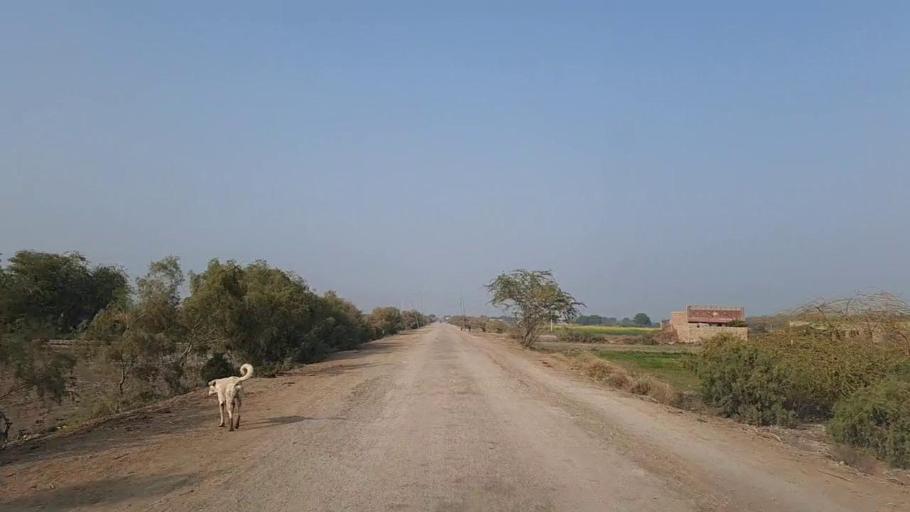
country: PK
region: Sindh
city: Nawabshah
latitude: 26.3325
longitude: 68.4890
